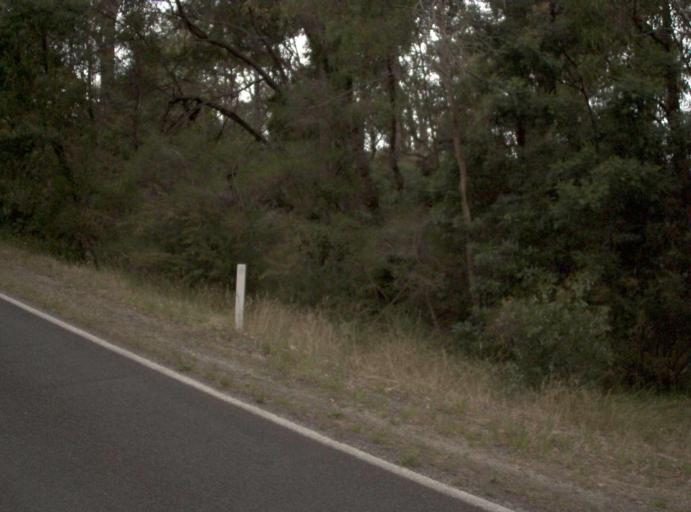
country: AU
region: Victoria
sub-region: Latrobe
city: Traralgon
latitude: -38.5390
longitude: 146.8444
